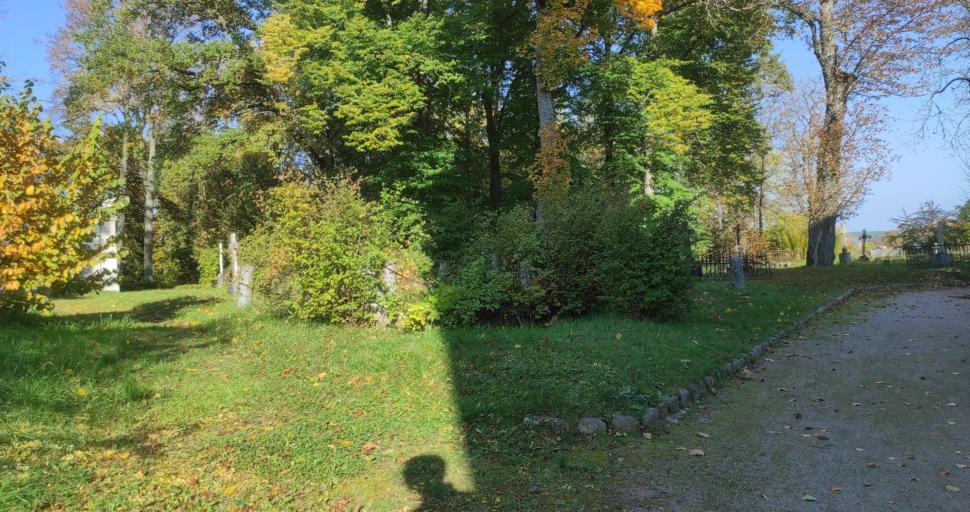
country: LV
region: Kandava
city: Kandava
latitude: 57.0365
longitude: 22.7718
